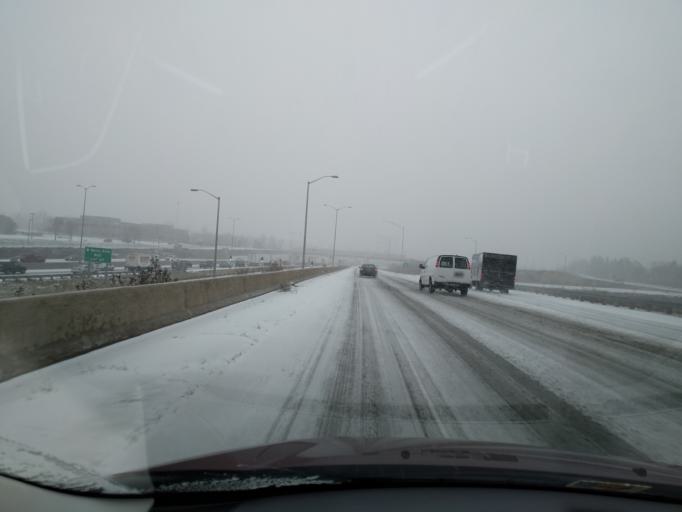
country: US
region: Wisconsin
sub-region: Waukesha County
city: Butler
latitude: 43.1577
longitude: -88.0618
